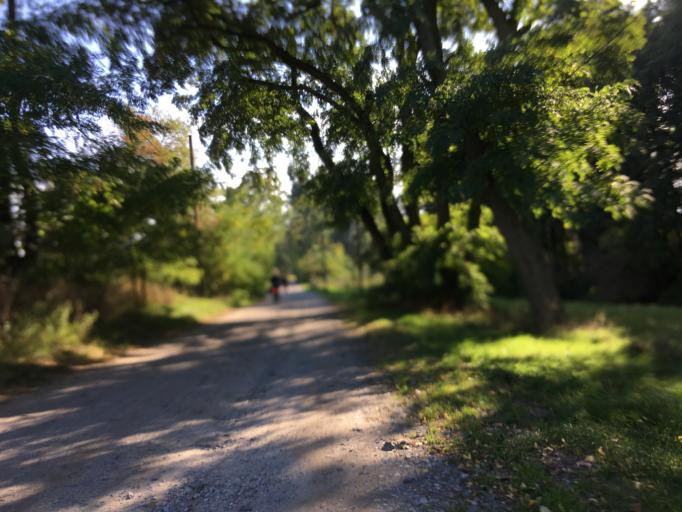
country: DE
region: Brandenburg
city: Altlandsberg
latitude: 52.5359
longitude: 13.7223
